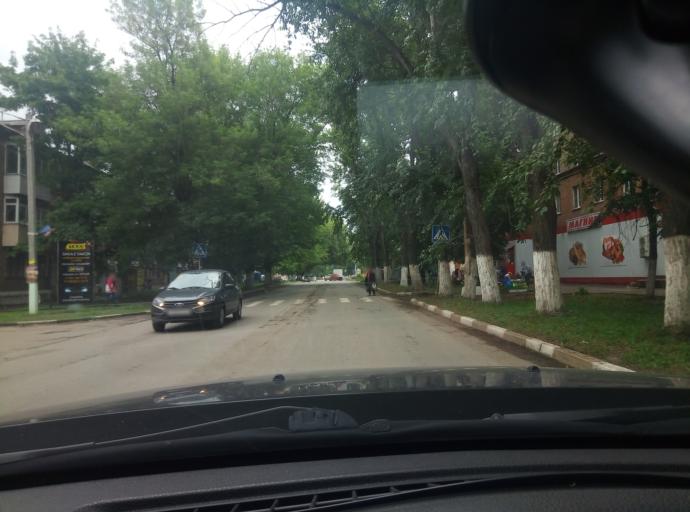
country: RU
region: Tula
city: Kimovsk
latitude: 53.9733
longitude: 38.5309
